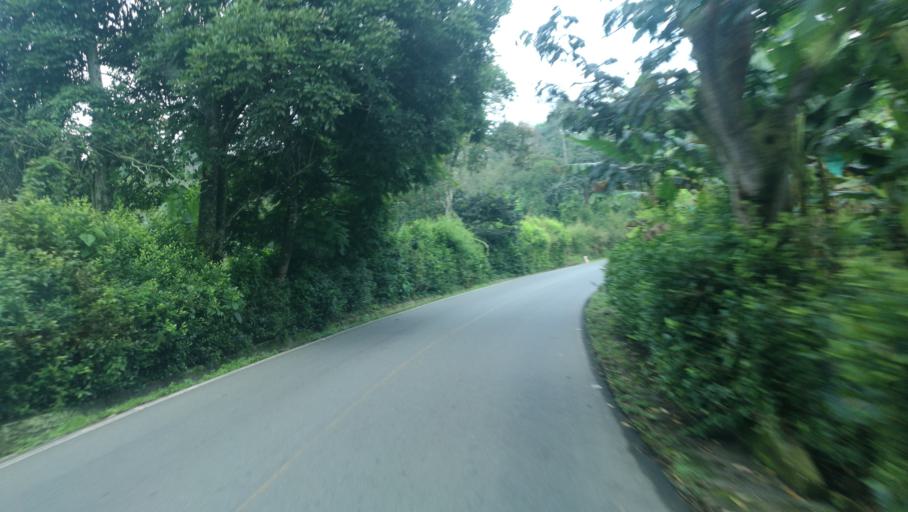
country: CO
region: Quindio
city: La Tebaida
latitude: 4.5080
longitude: -75.7835
